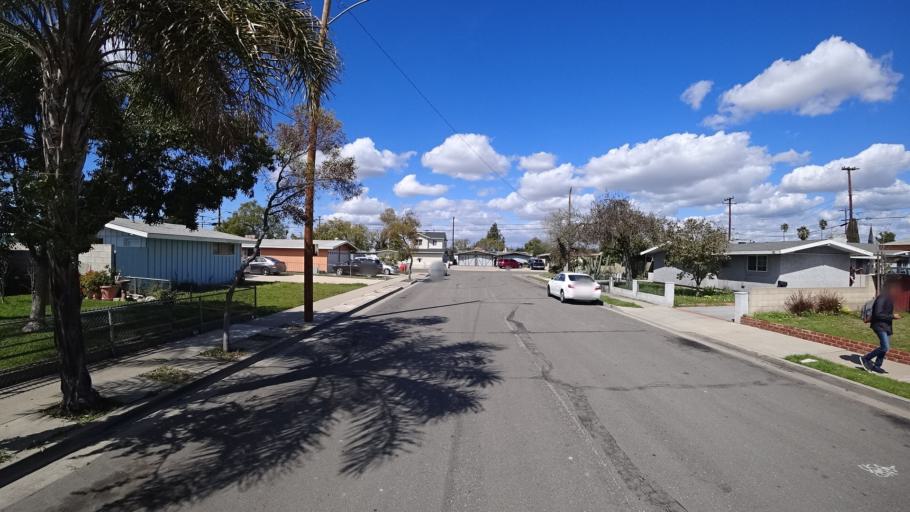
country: US
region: California
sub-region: Orange County
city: Anaheim
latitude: 33.8348
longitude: -117.8911
